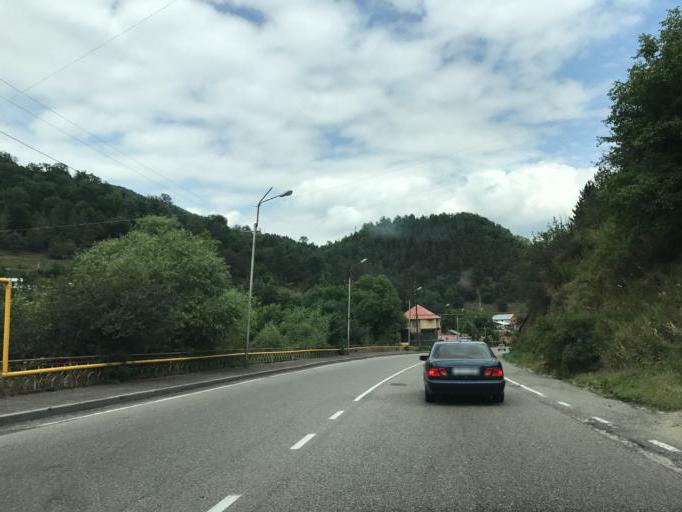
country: AM
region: Tavush
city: Dilijan
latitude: 40.7076
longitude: 44.8504
